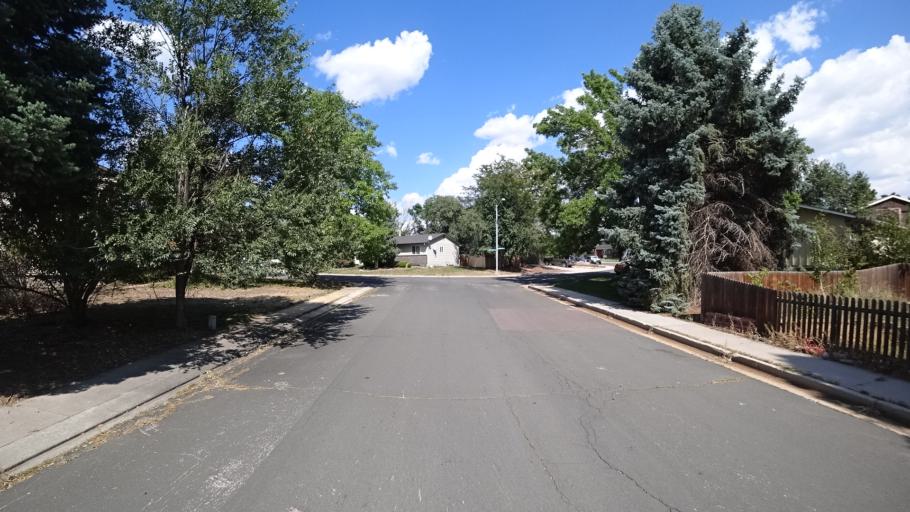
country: US
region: Colorado
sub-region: El Paso County
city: Cimarron Hills
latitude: 38.8732
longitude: -104.7517
